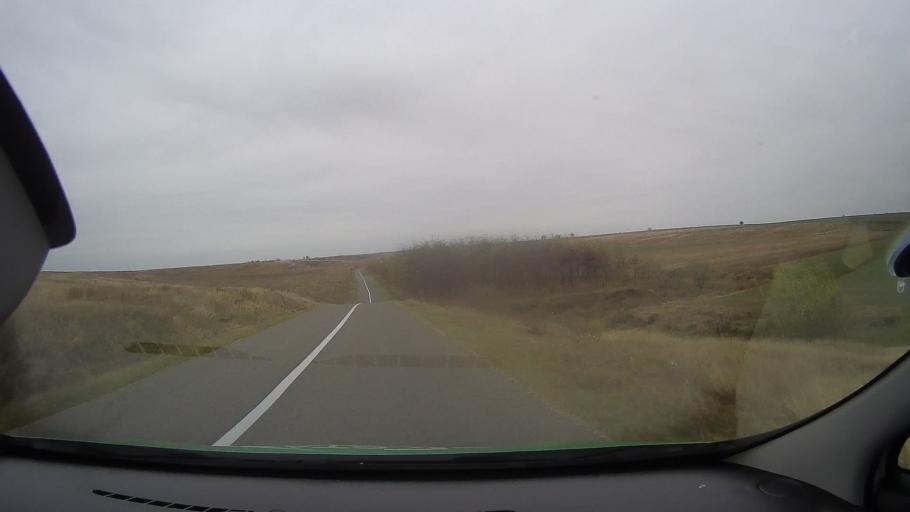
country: RO
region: Constanta
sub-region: Comuna Saraiu
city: Saraiu
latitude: 44.7262
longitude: 28.1801
